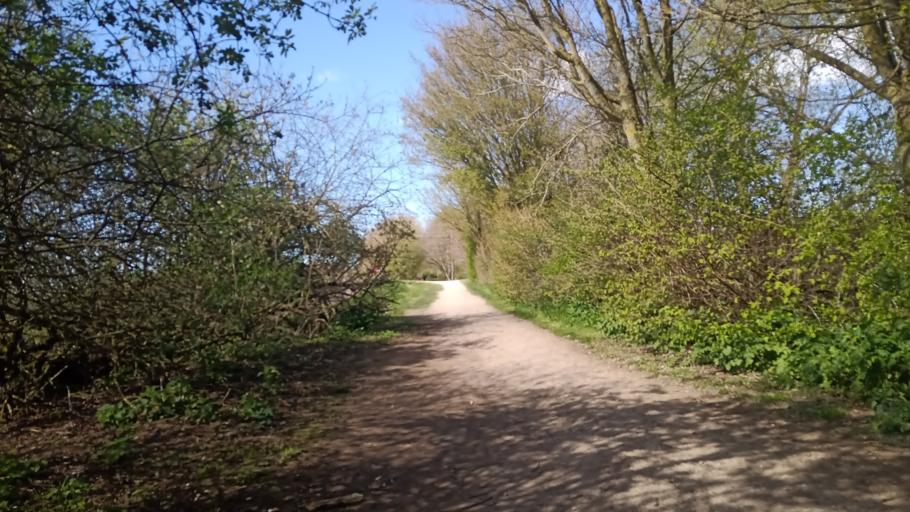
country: GB
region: England
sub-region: Oxfordshire
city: Ducklington
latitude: 51.7712
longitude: -1.4829
